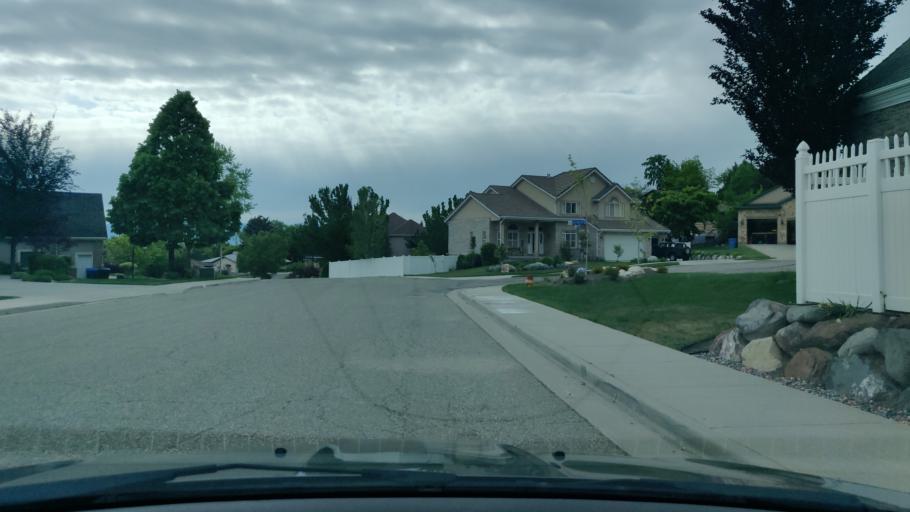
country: US
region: Utah
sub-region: Salt Lake County
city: Cottonwood Heights
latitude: 40.6070
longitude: -111.8143
